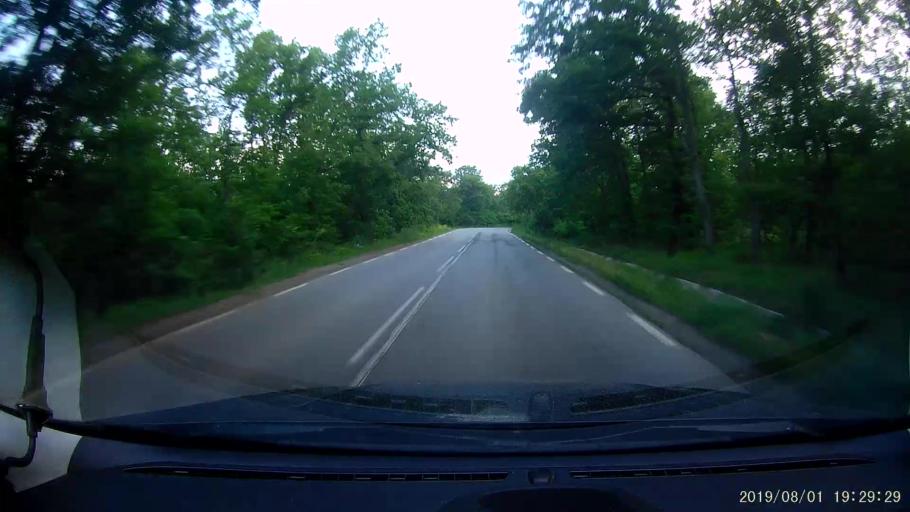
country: BG
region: Burgas
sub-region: Obshtina Sungurlare
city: Sungurlare
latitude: 42.8250
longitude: 26.9067
